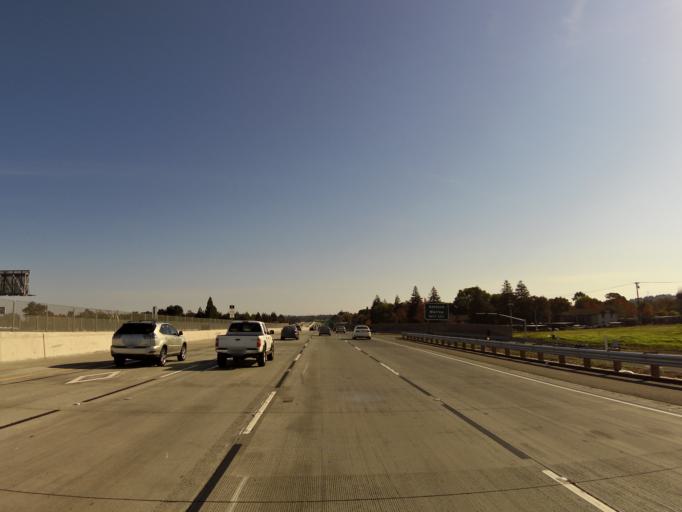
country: US
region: California
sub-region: Contra Costa County
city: Antioch
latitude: 38.0035
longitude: -121.8370
